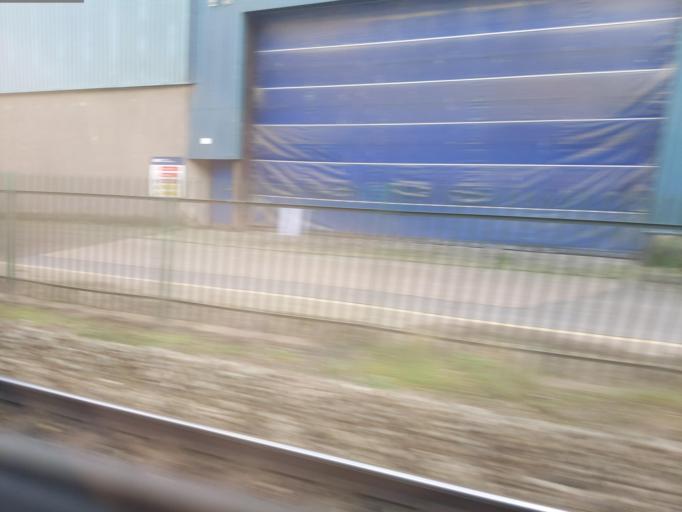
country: GB
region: England
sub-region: Devon
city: Teignmouth
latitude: 50.5466
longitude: -3.5040
